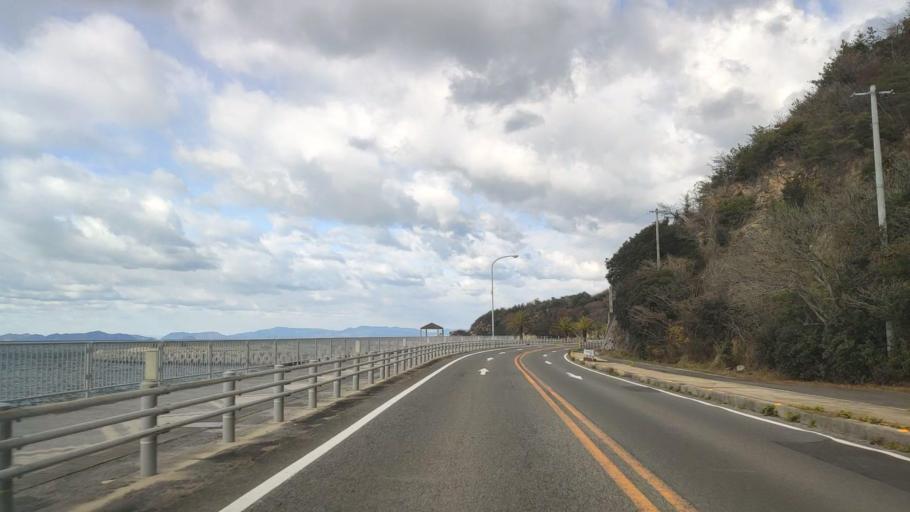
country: JP
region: Ehime
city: Hojo
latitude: 33.9930
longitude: 132.7737
